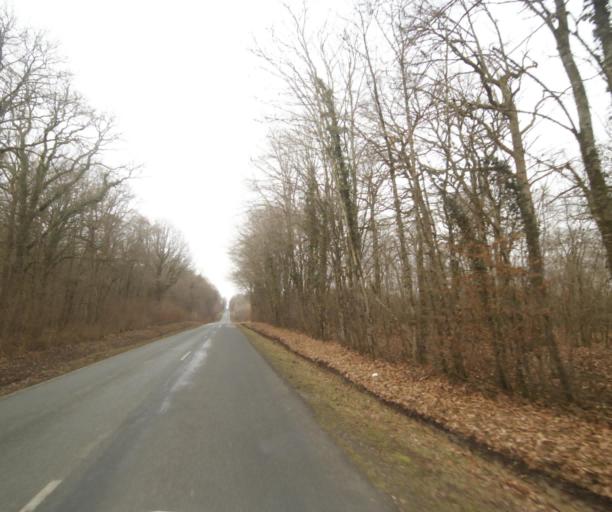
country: FR
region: Champagne-Ardenne
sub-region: Departement de la Haute-Marne
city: Villiers-en-Lieu
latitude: 48.7125
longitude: 4.8858
